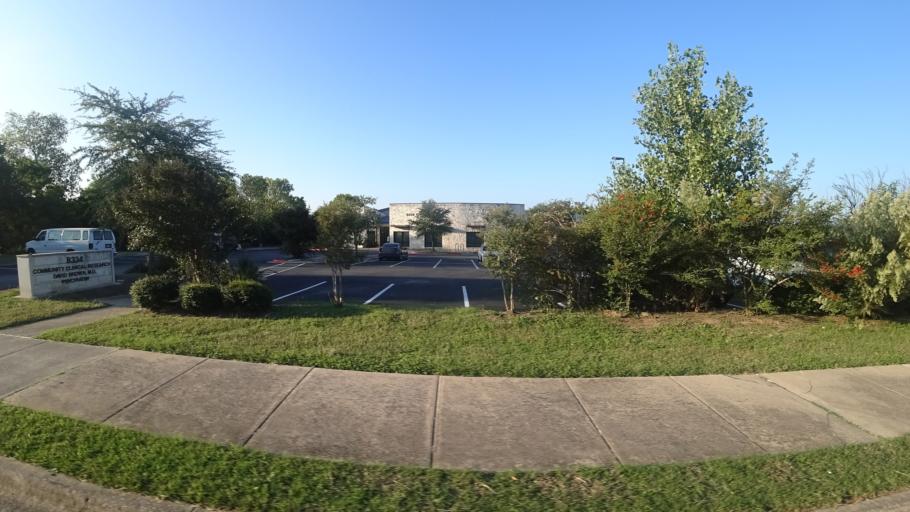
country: US
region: Texas
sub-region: Travis County
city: Austin
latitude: 30.3363
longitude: -97.6754
